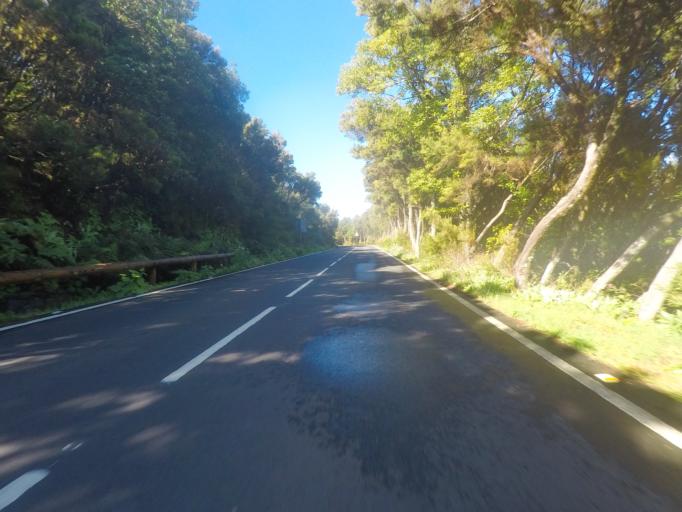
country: ES
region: Canary Islands
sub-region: Provincia de Santa Cruz de Tenerife
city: Alajero
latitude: 28.1075
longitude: -17.2360
